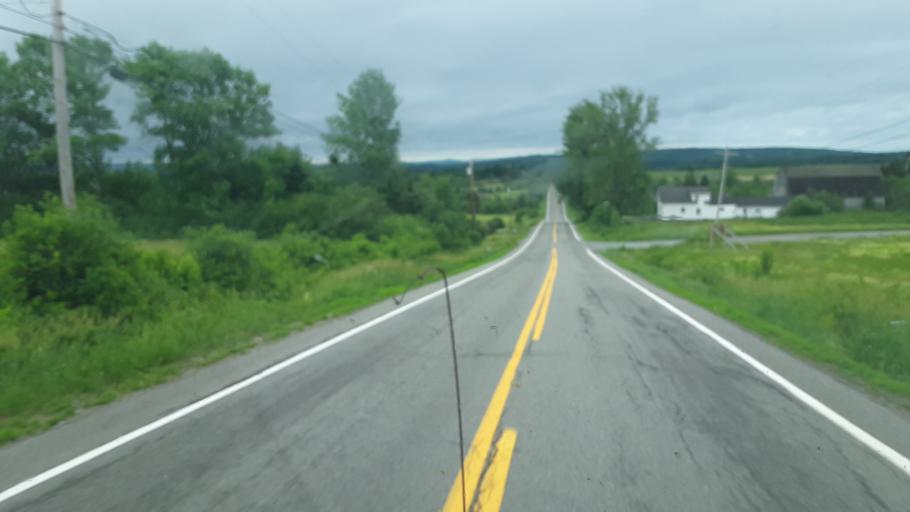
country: US
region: Maine
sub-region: Penobscot County
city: Patten
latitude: 46.0250
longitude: -68.4452
